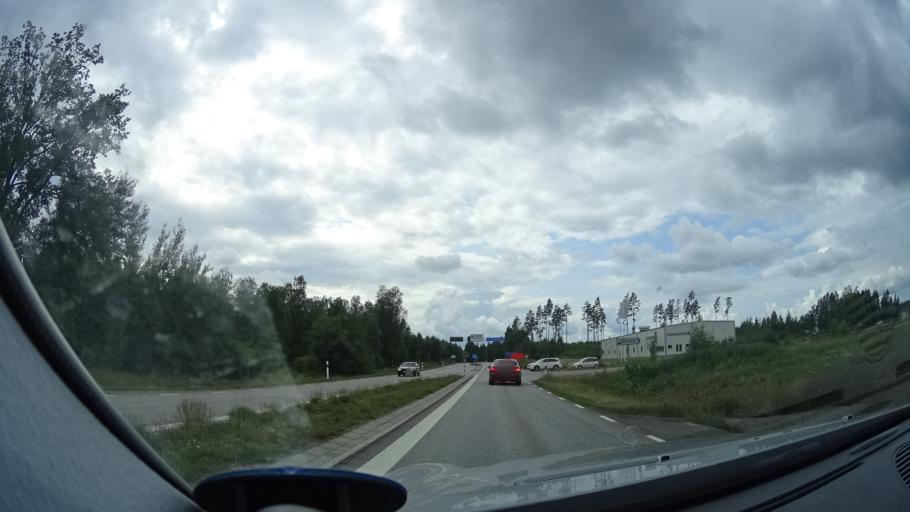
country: SE
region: Kronoberg
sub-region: Tingsryds Kommun
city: Tingsryd
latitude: 56.5141
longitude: 14.9976
